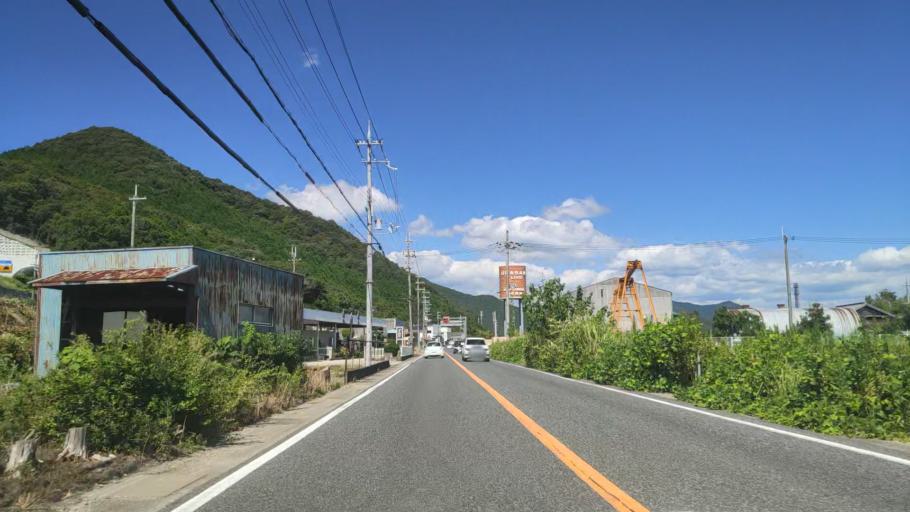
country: JP
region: Hyogo
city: Nishiwaki
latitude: 35.0129
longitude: 134.9900
